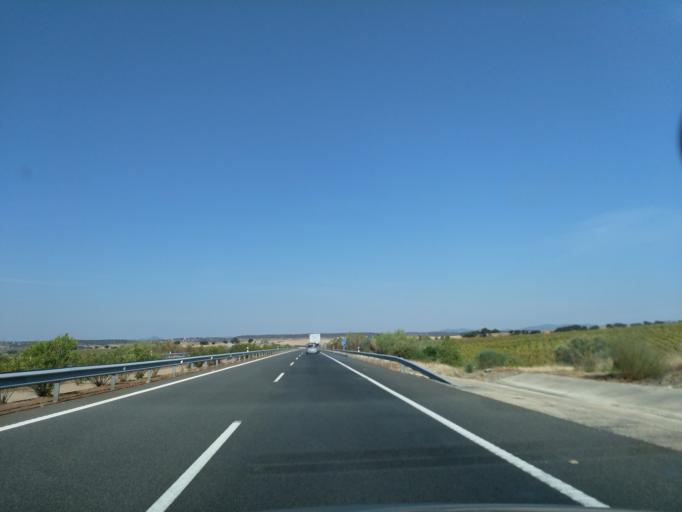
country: ES
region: Extremadura
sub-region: Provincia de Badajoz
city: Aljucen
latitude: 39.0308
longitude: -6.3352
